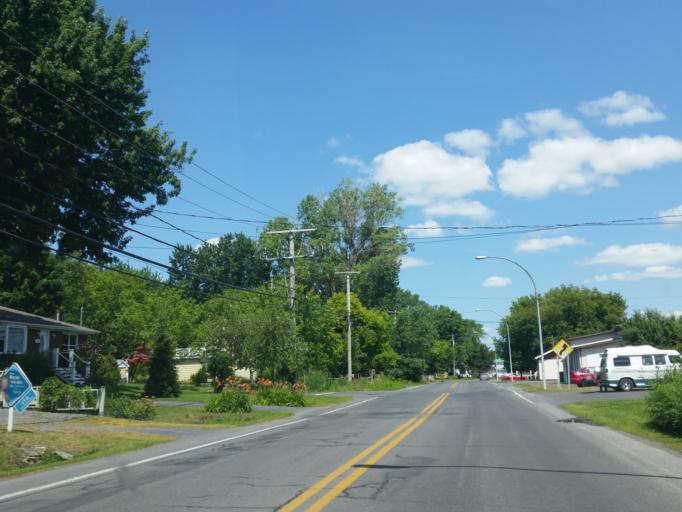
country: CA
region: Quebec
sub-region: Monteregie
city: Saint-Jean-sur-Richelieu
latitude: 45.3518
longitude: -73.2674
